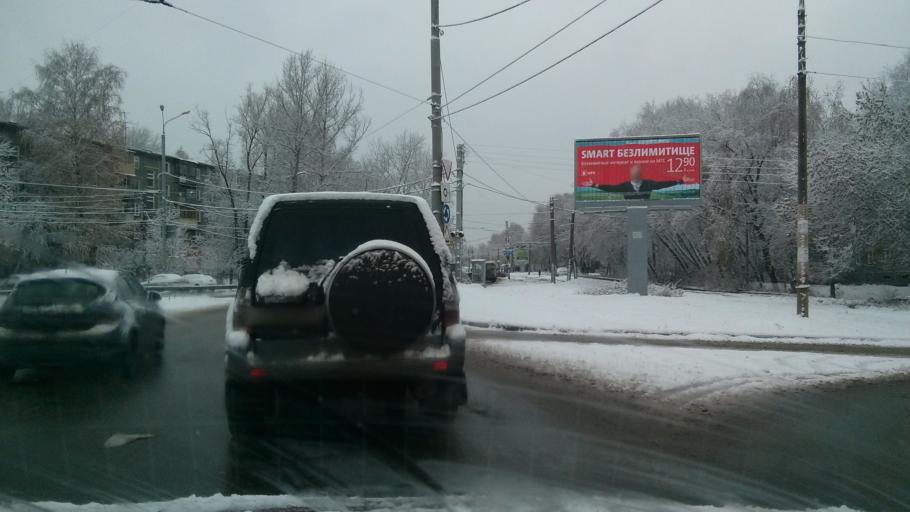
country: RU
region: Nizjnij Novgorod
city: Nizhniy Novgorod
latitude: 56.3032
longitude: 44.0454
